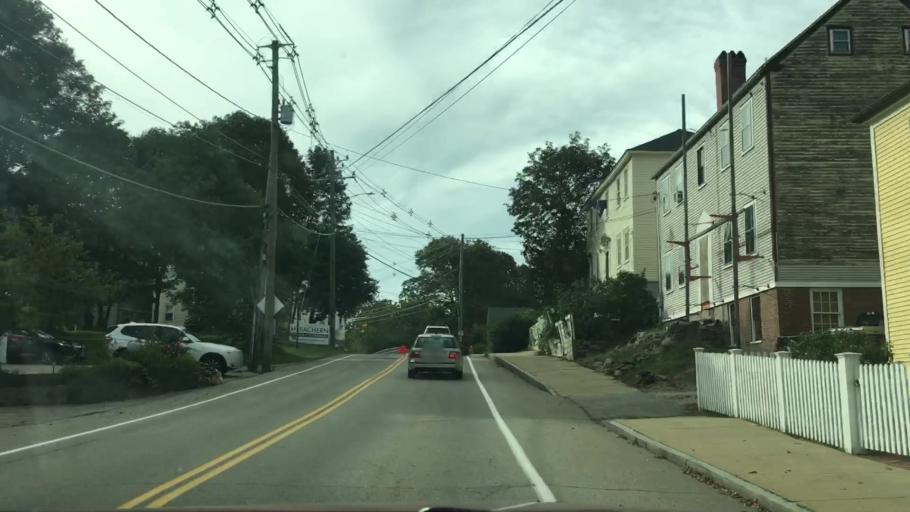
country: US
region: New Hampshire
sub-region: Rockingham County
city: Portsmouth
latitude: 43.0802
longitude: -70.7676
